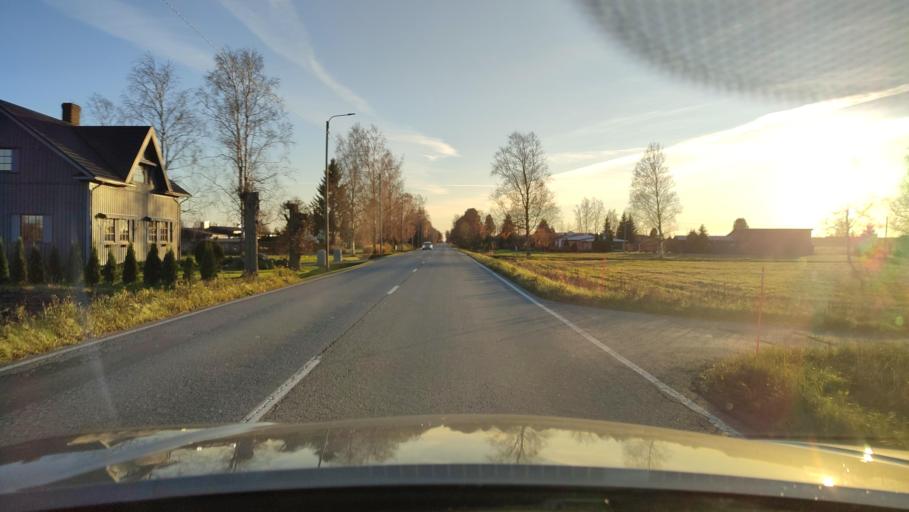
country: FI
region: Ostrobothnia
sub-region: Sydosterbotten
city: Naerpes
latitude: 62.5988
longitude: 21.4529
